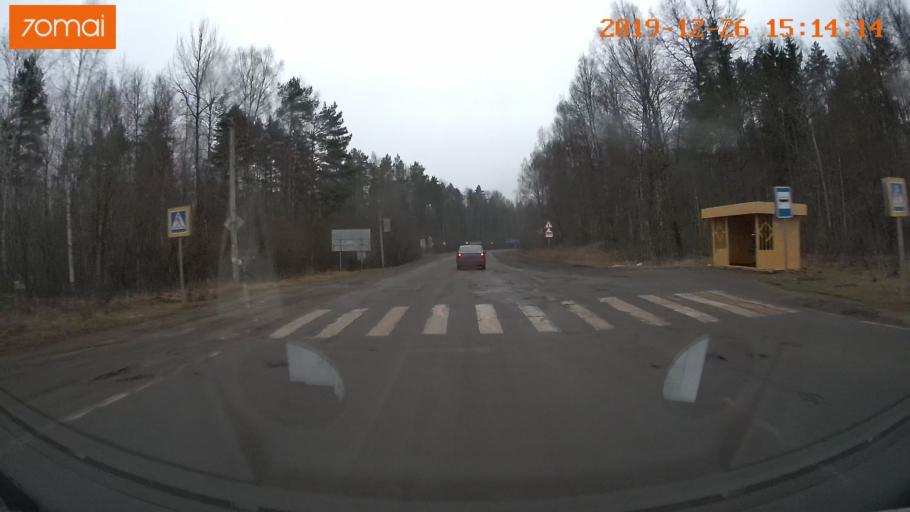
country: RU
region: Jaroslavl
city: Rybinsk
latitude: 58.1078
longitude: 38.8815
